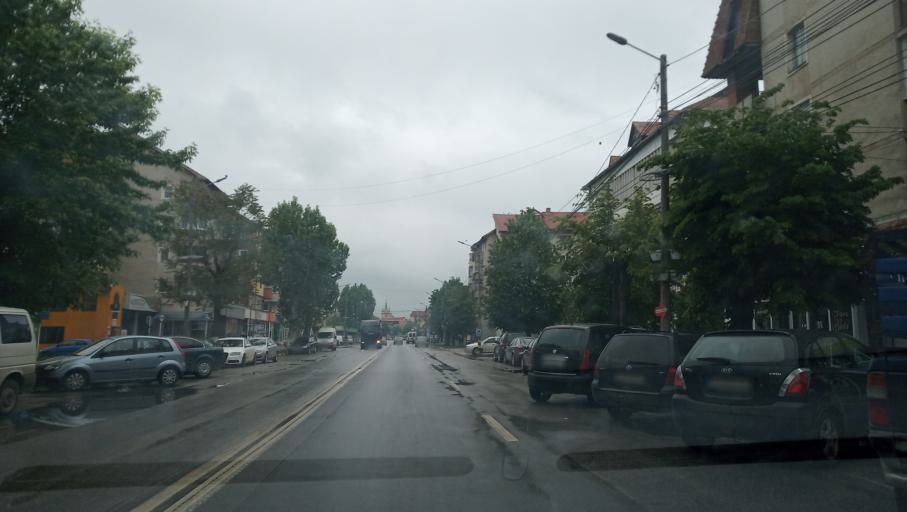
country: RO
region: Alba
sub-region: Municipiul Sebes
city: Sebes
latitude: 45.9559
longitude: 23.5769
